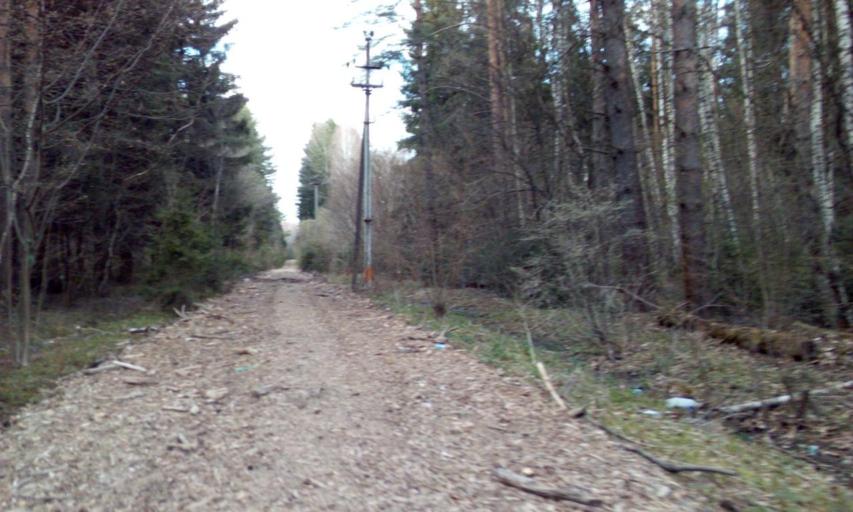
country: RU
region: Moskovskaya
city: Annino
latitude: 55.5368
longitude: 37.2228
